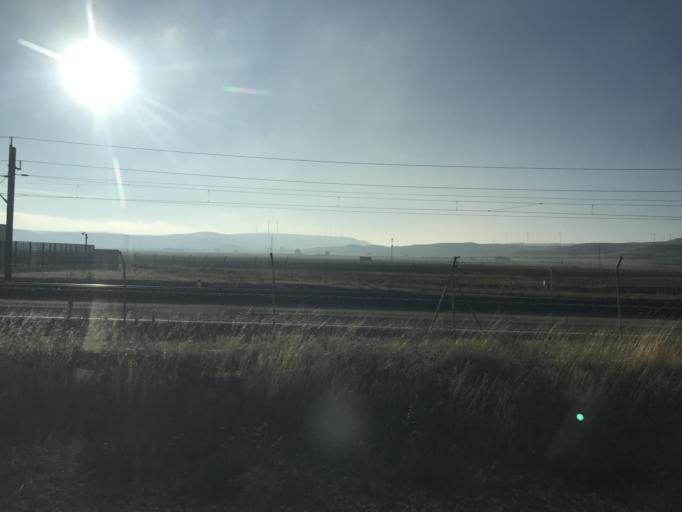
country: ES
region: Castille and Leon
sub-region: Provincia de Palencia
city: Quintana del Puente
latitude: 42.0626
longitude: -4.2257
